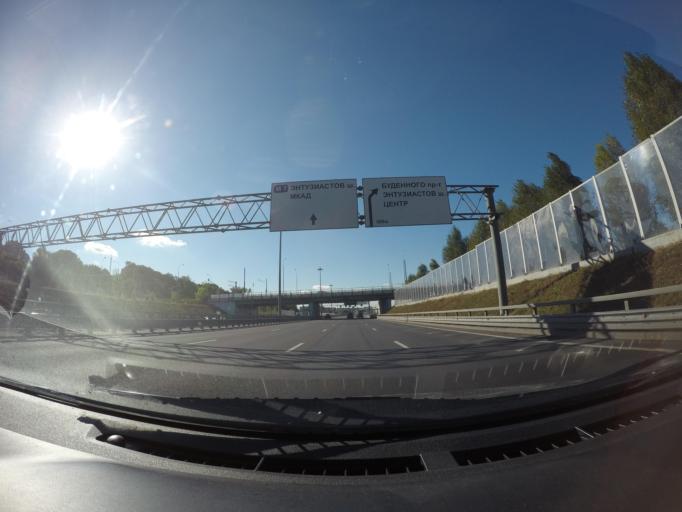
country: RU
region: Moscow
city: Ryazanskiy
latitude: 55.7697
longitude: 37.7467
